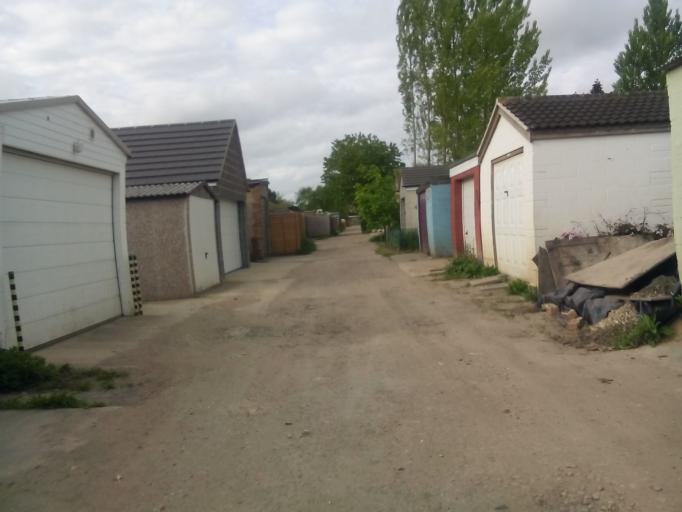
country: GB
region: England
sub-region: Cambridgeshire
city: Cambridge
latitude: 52.2040
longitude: 0.1484
